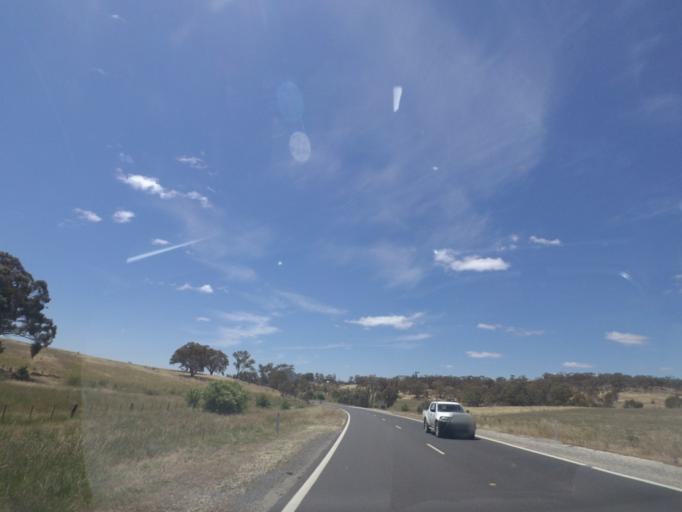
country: AU
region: Victoria
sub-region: Mount Alexander
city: Castlemaine
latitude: -37.1613
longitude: 144.1571
